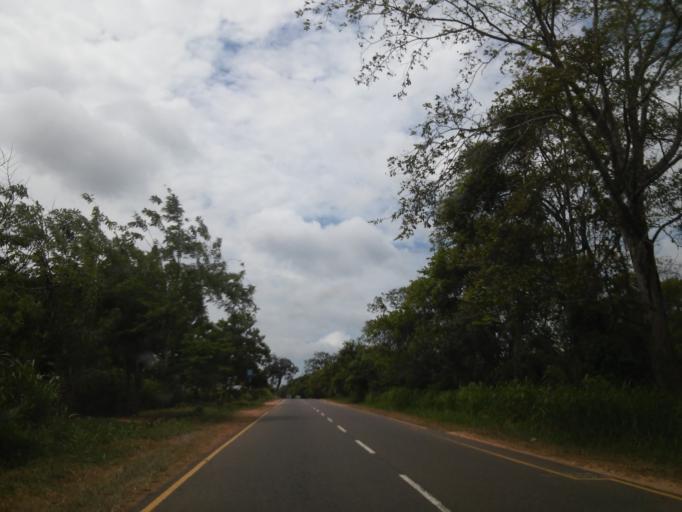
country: LK
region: Central
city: Sigiriya
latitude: 8.0493
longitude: 80.7284
